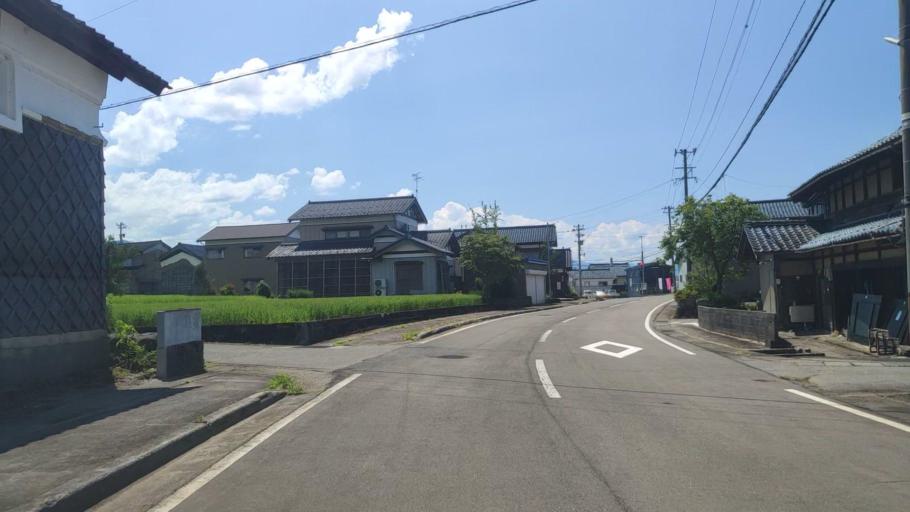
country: JP
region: Fukui
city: Katsuyama
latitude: 36.0910
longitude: 136.4912
